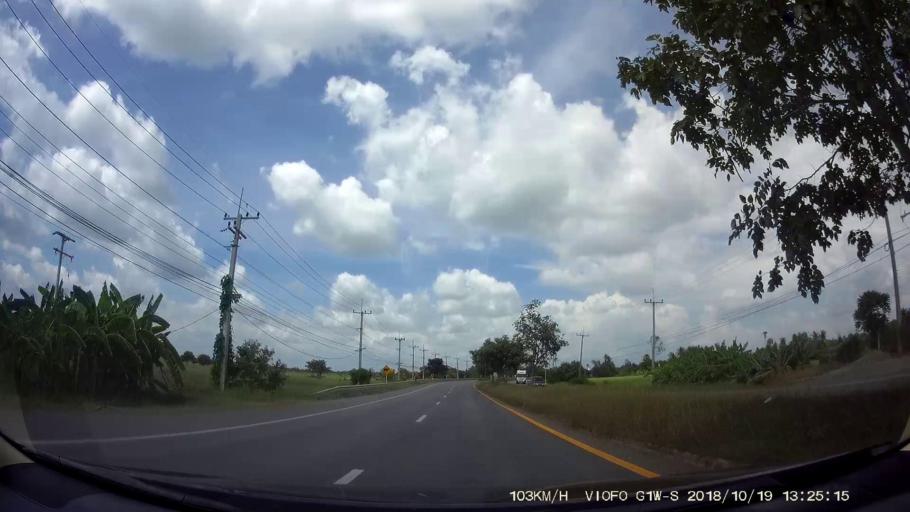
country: TH
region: Chaiyaphum
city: Chatturat
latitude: 15.5187
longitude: 101.8252
